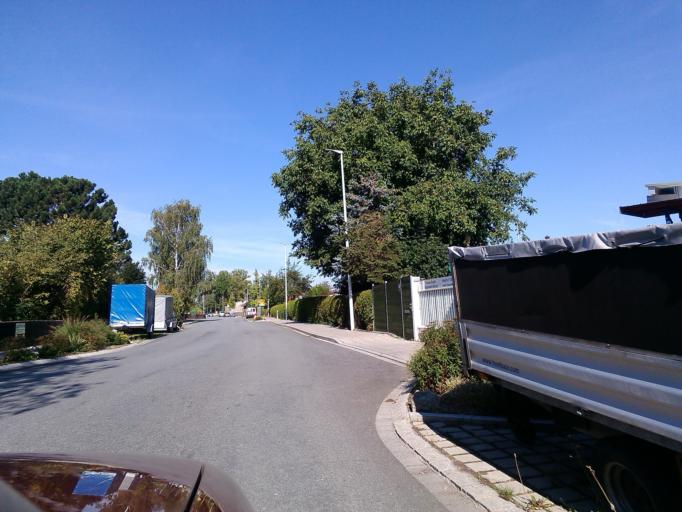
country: DE
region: Bavaria
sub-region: Upper Bavaria
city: Puchheim
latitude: 48.1486
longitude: 11.3429
